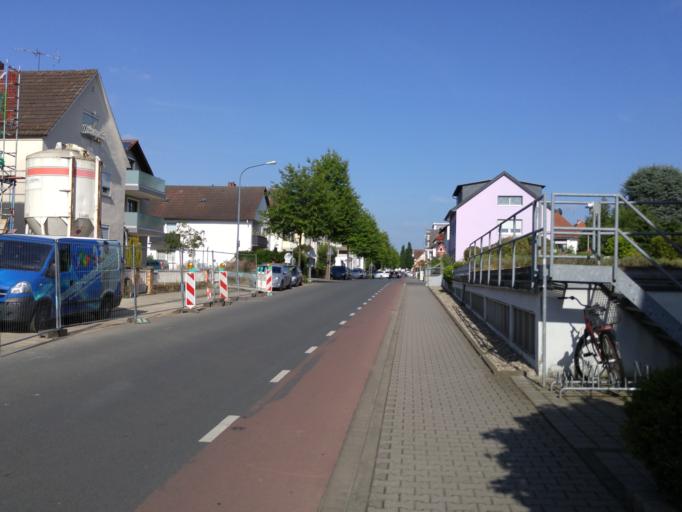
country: DE
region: Hesse
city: Langen
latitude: 49.9932
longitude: 8.6611
